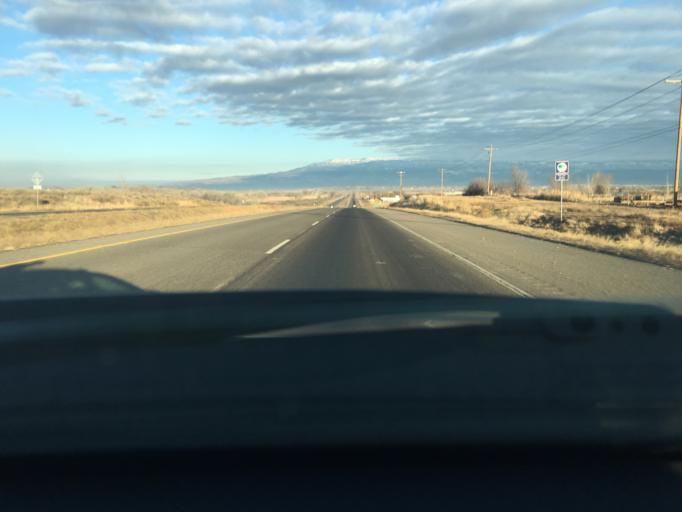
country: US
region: Colorado
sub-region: Montrose County
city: Olathe
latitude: 38.6656
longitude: -107.9968
